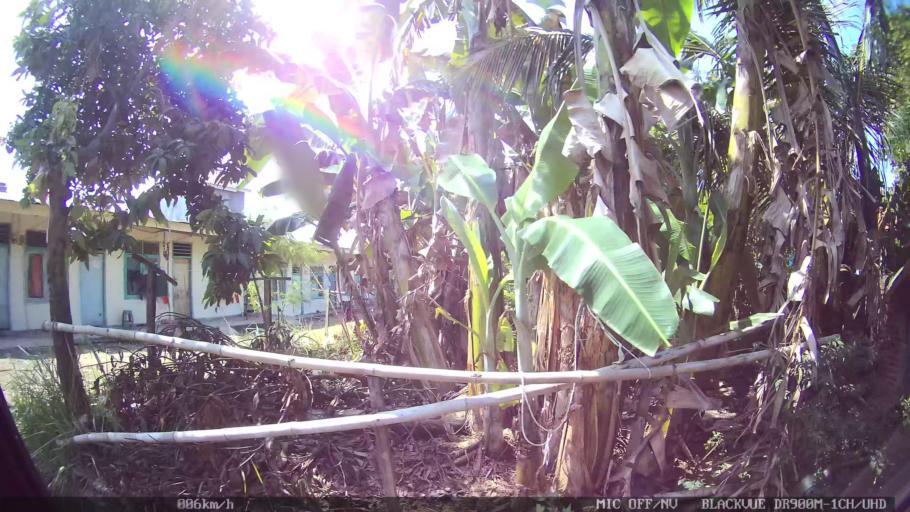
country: ID
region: Lampung
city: Kedaton
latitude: -5.3650
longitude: 105.2561
